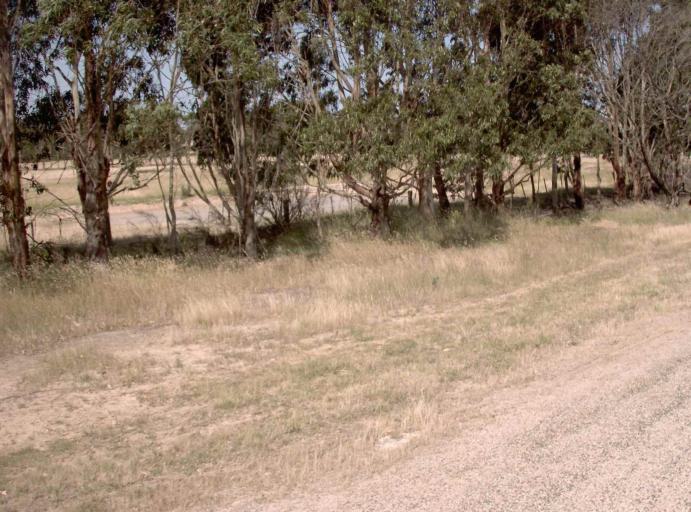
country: AU
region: Victoria
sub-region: Wellington
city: Sale
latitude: -38.3435
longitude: 147.1699
